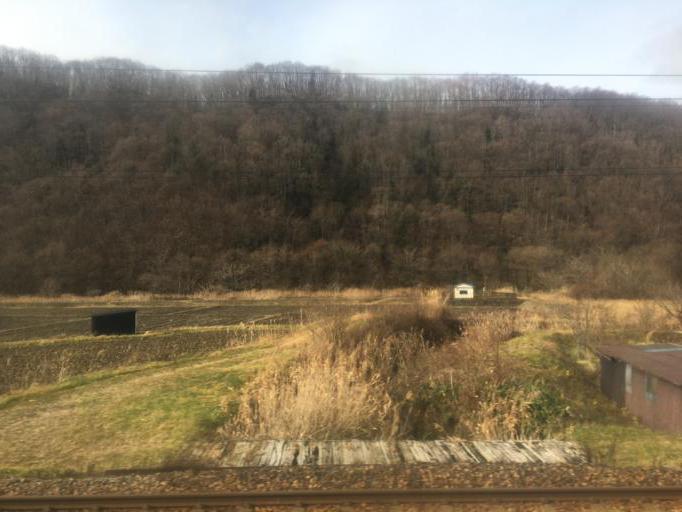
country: JP
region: Akita
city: Odate
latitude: 40.3502
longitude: 140.5984
